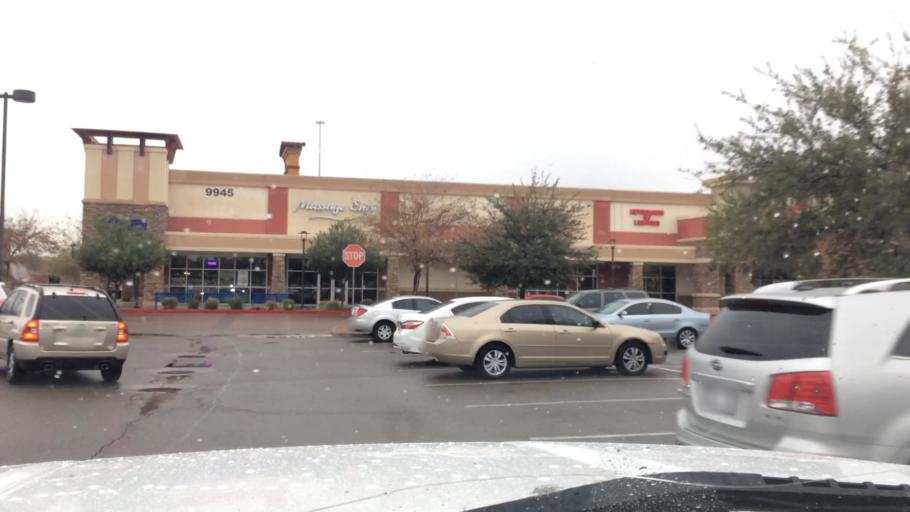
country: US
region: Arizona
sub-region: Maricopa County
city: Tolleson
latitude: 33.4640
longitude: -112.2737
